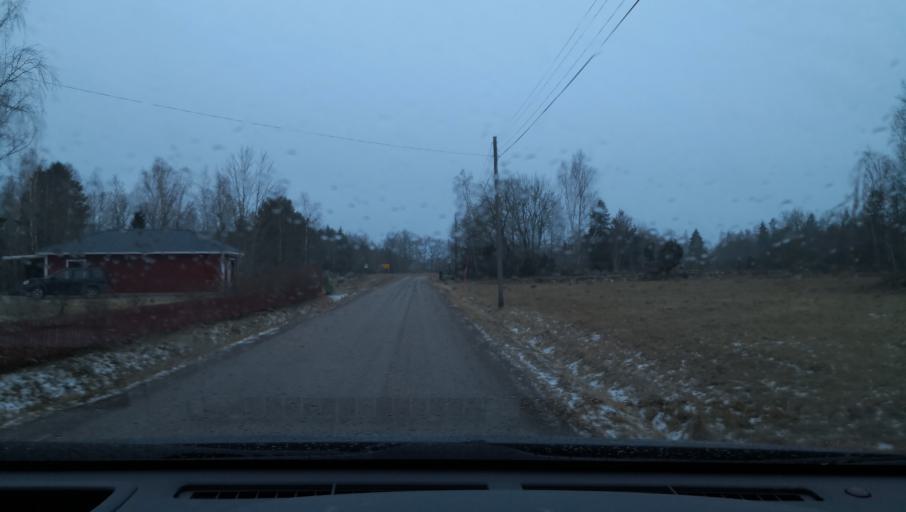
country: SE
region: Uppsala
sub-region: Enkopings Kommun
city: Hummelsta
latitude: 59.4577
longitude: 16.8261
